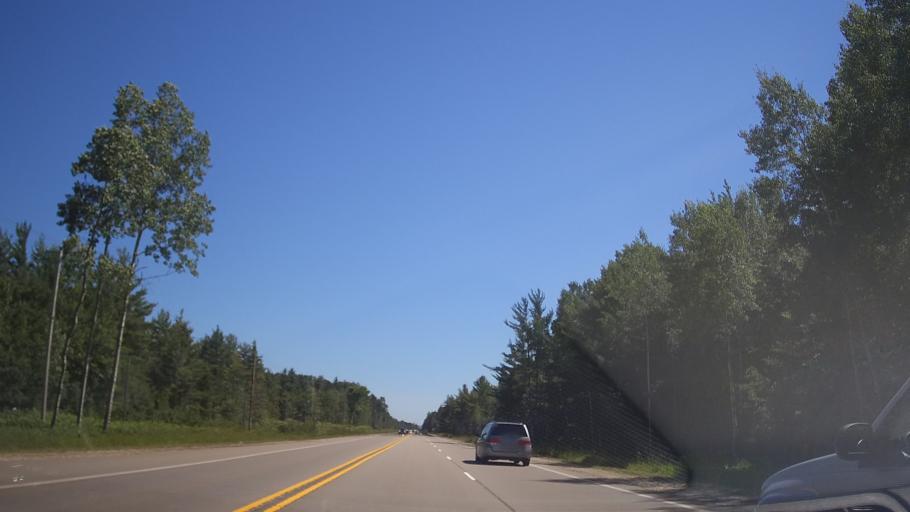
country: US
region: Michigan
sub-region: Cheboygan County
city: Indian River
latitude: 45.5263
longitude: -84.7818
